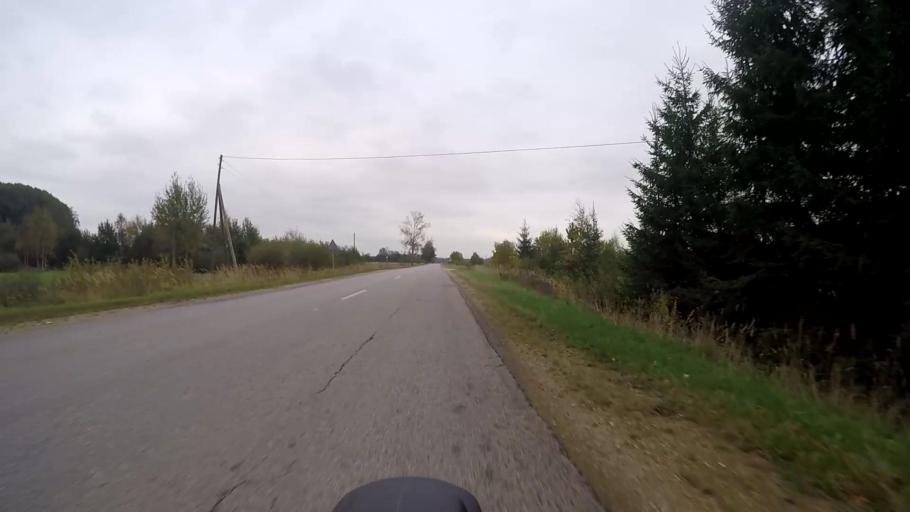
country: LV
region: Saulkrastu
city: Saulkrasti
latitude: 57.2743
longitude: 24.5259
